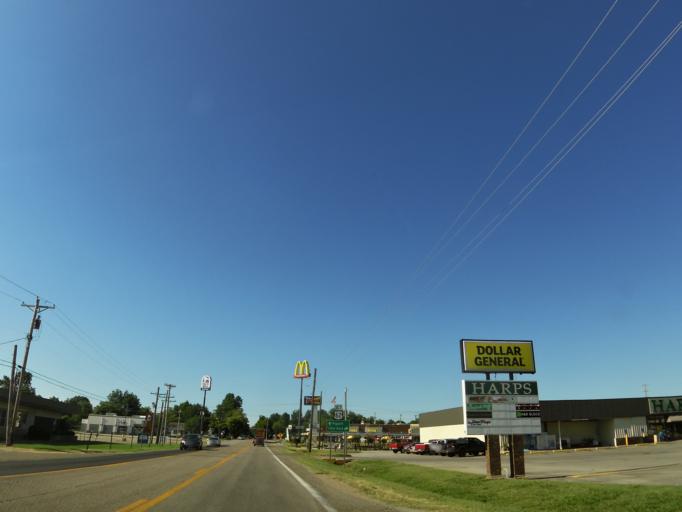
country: US
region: Arkansas
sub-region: Clay County
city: Corning
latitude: 36.4143
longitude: -90.5864
